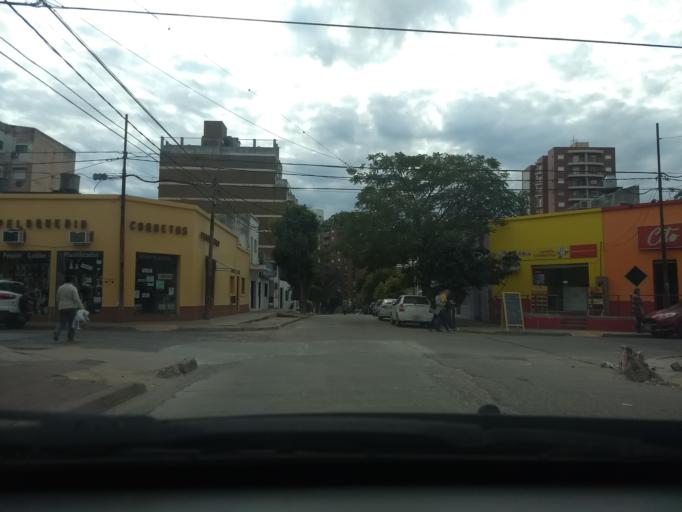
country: AR
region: Corrientes
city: Corrientes
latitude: -27.4690
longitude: -58.8228
